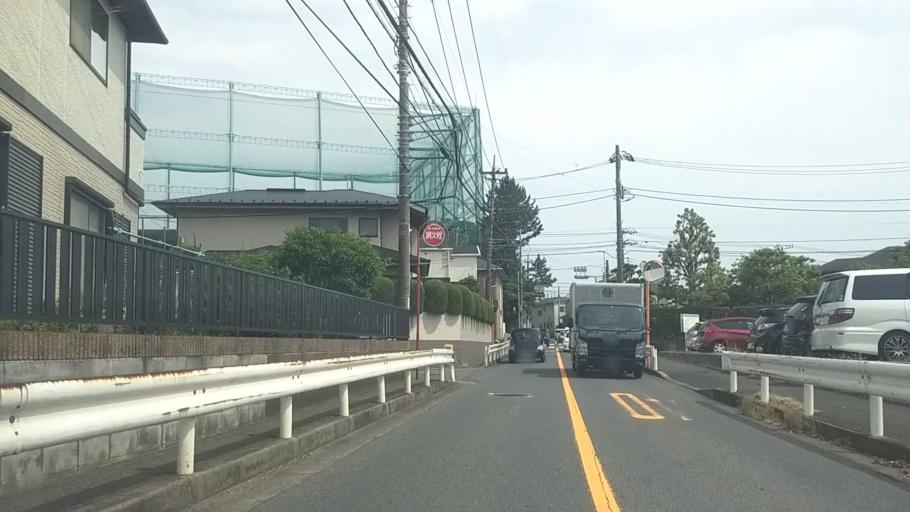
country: JP
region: Kanagawa
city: Fujisawa
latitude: 35.3893
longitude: 139.4625
